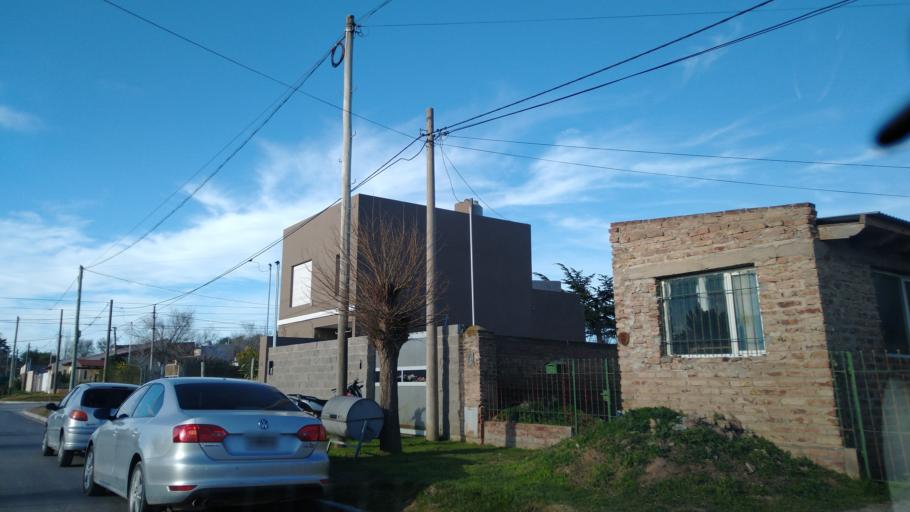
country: AR
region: Buenos Aires
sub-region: Partido de Bahia Blanca
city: Bahia Blanca
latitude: -38.7018
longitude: -62.2097
